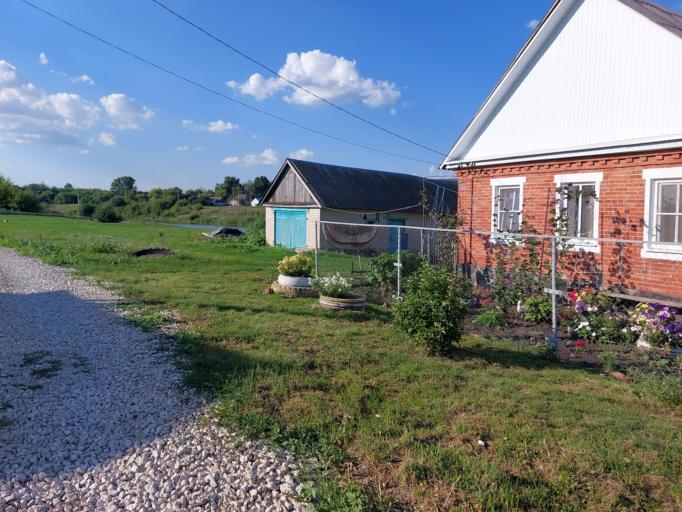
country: RU
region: Lipetsk
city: Terbuny
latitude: 52.2745
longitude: 38.1966
